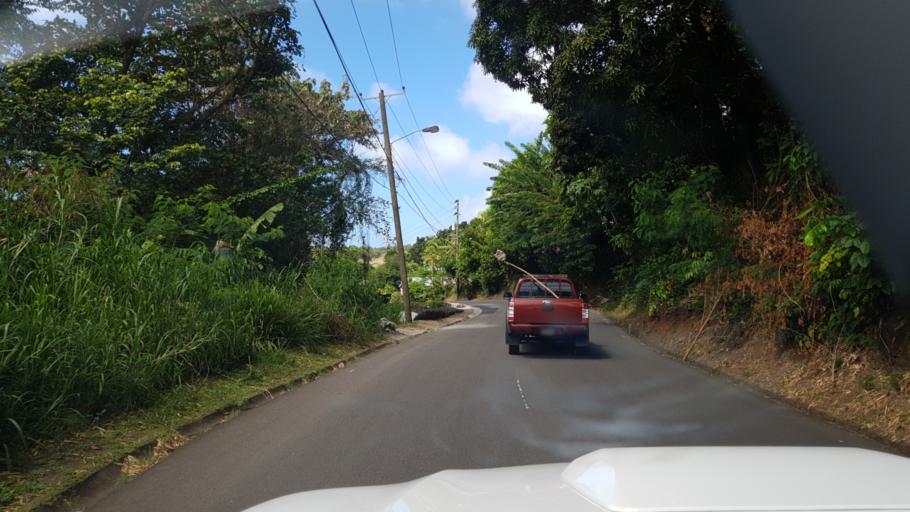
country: LC
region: Castries Quarter
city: Bisee
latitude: 14.0194
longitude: -60.9596
